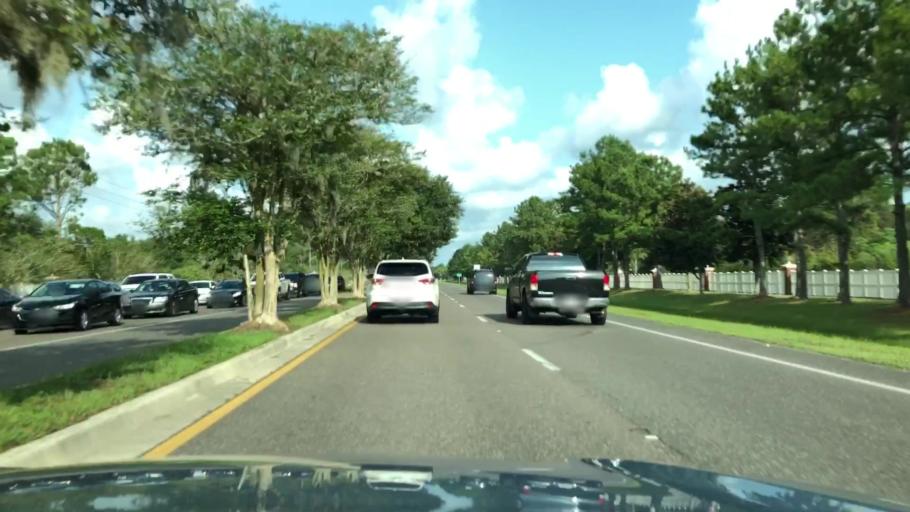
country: US
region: Florida
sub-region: Saint Johns County
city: Fruit Cove
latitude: 30.1184
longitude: -81.6101
